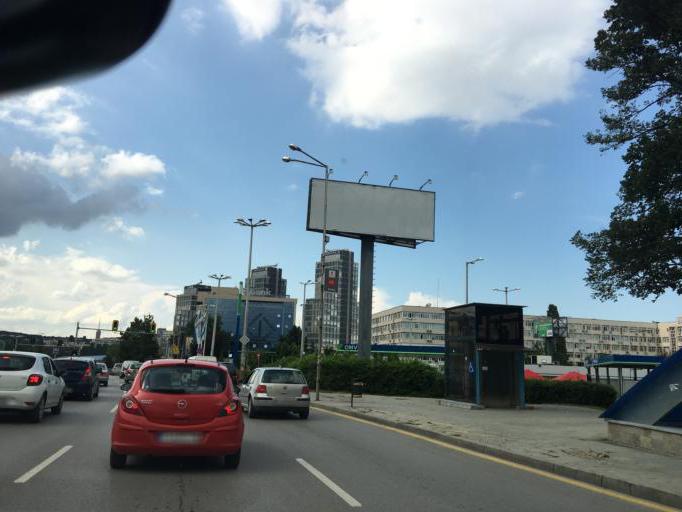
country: BG
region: Sofia-Capital
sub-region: Stolichna Obshtina
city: Sofia
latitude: 42.6626
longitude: 23.3585
